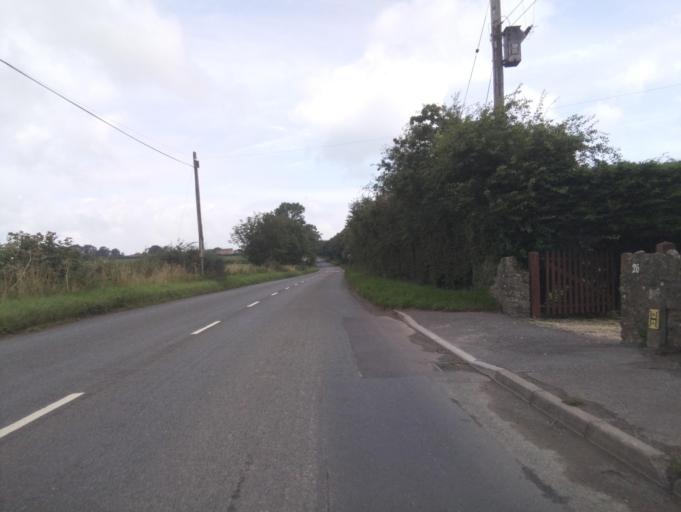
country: GB
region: England
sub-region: Somerset
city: Evercreech
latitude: 51.1911
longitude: -2.4832
